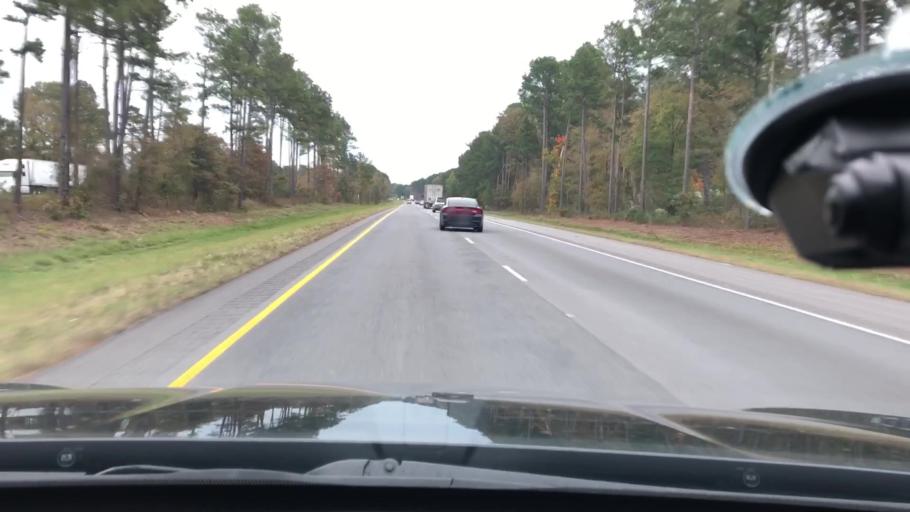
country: US
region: Arkansas
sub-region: Hempstead County
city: Hope
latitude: 33.6275
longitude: -93.7411
